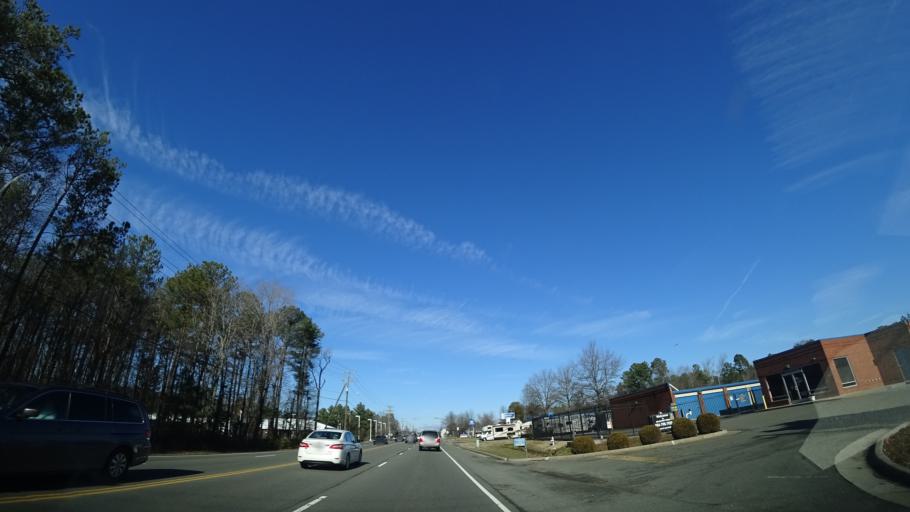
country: US
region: Virginia
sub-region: Hanover County
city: Ashland
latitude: 37.7487
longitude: -77.4713
